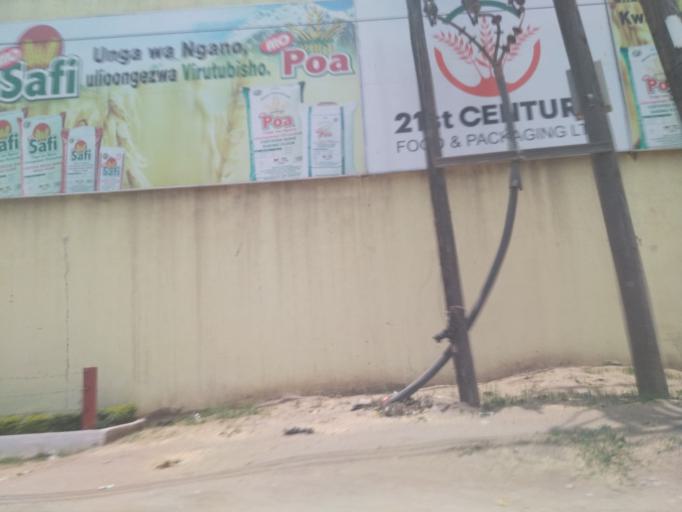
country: TZ
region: Dar es Salaam
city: Dar es Salaam
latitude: -6.8358
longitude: 39.2908
